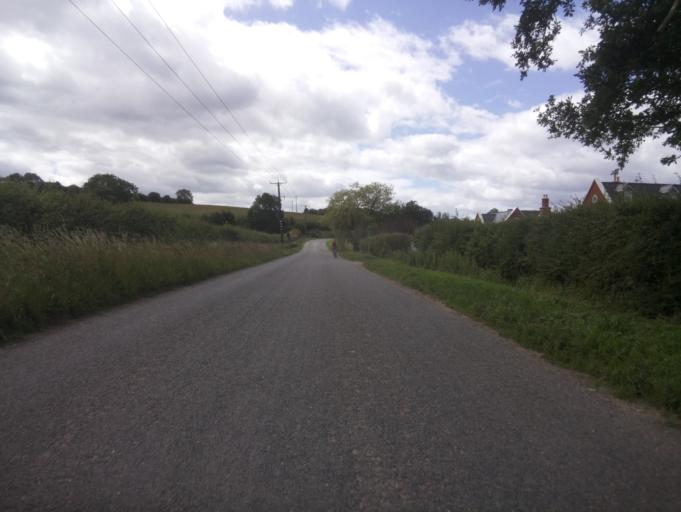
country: GB
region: England
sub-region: Nottinghamshire
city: Ruddington
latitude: 52.8572
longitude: -1.1004
